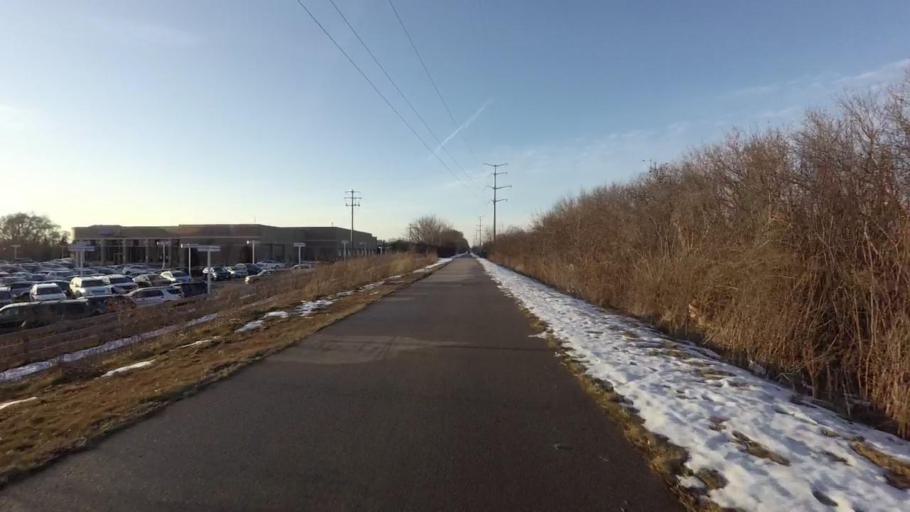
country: US
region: Wisconsin
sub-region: Milwaukee County
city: Glendale
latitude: 43.1190
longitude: -87.9315
